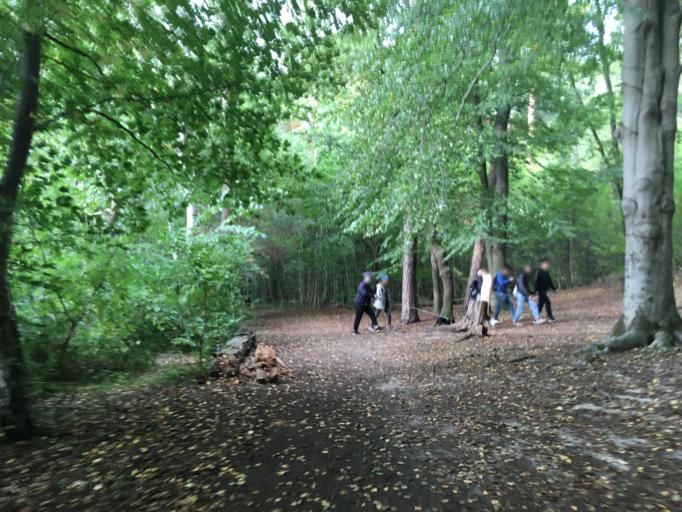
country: DE
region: Berlin
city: Blankenfelde
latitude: 52.6950
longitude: 13.3784
